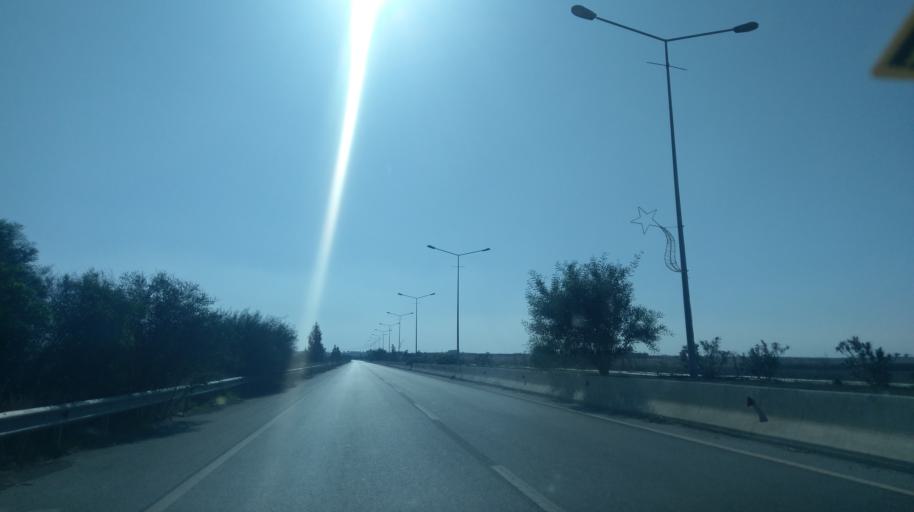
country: CY
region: Lefkosia
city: Geri
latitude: 35.1853
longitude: 33.5028
